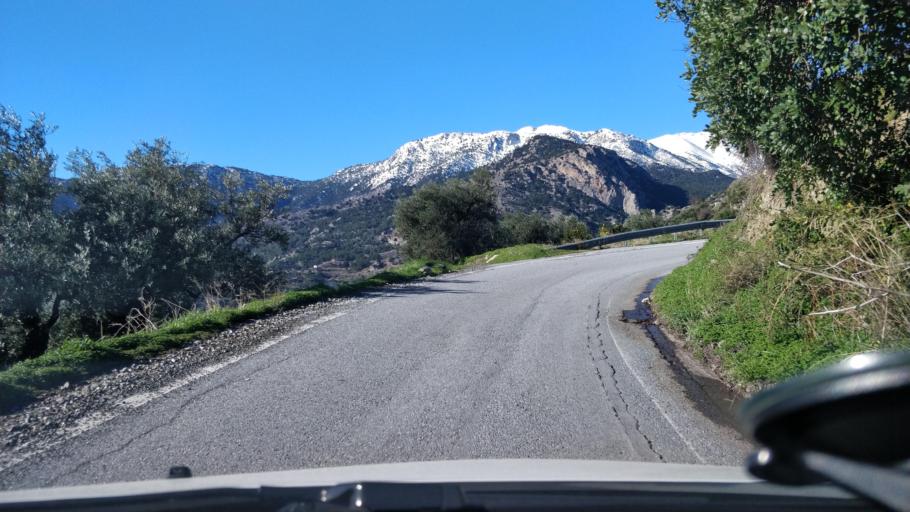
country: GR
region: Crete
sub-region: Nomos Lasithiou
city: Kritsa
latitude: 35.0776
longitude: 25.5820
